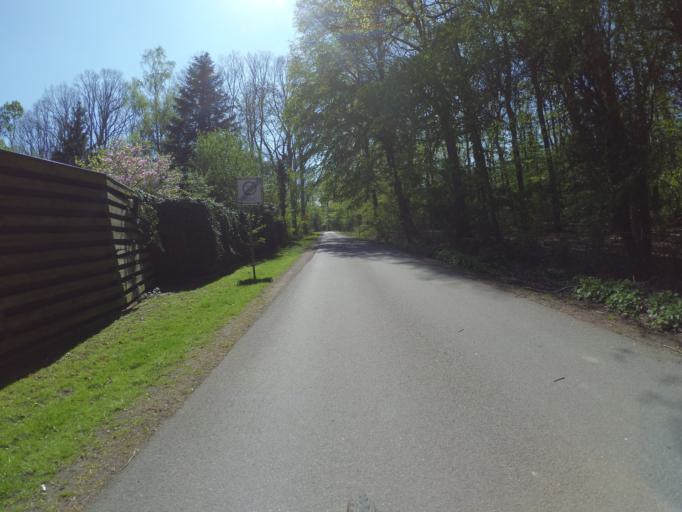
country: DE
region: North Rhine-Westphalia
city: Ludinghausen
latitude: 51.7609
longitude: 7.4386
